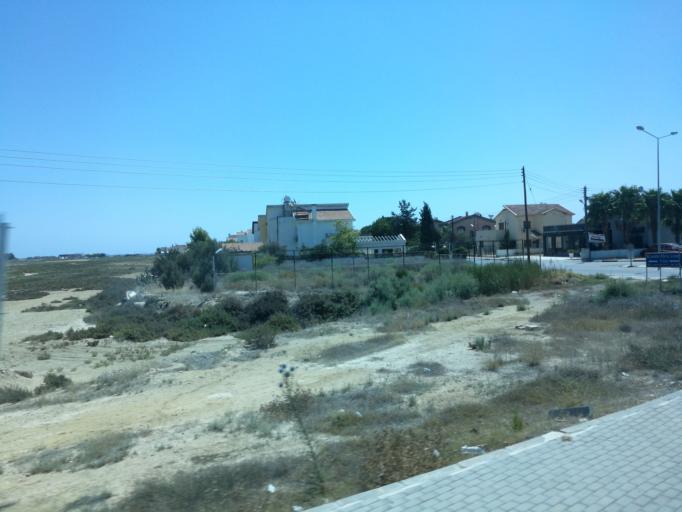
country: CY
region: Ammochostos
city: Famagusta
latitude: 35.1573
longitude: 33.9032
